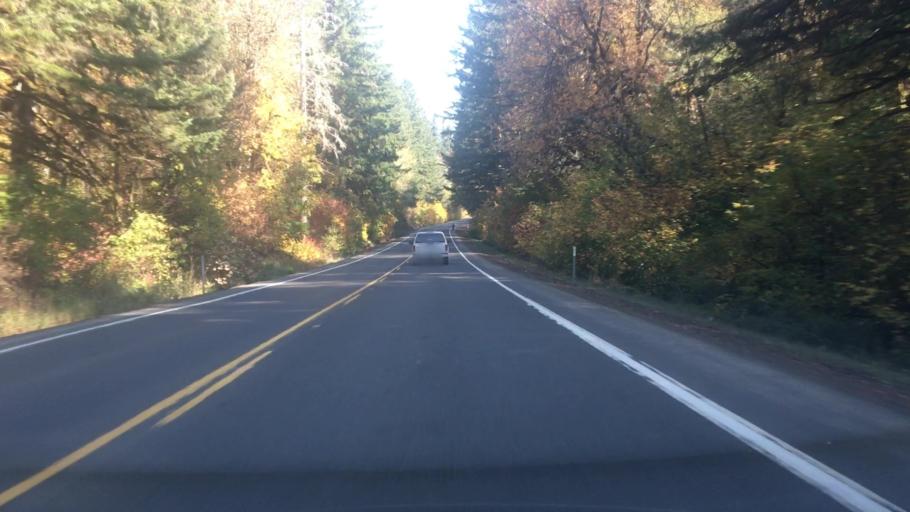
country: US
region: Oregon
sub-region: Polk County
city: Grand Ronde
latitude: 45.0604
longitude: -123.6705
